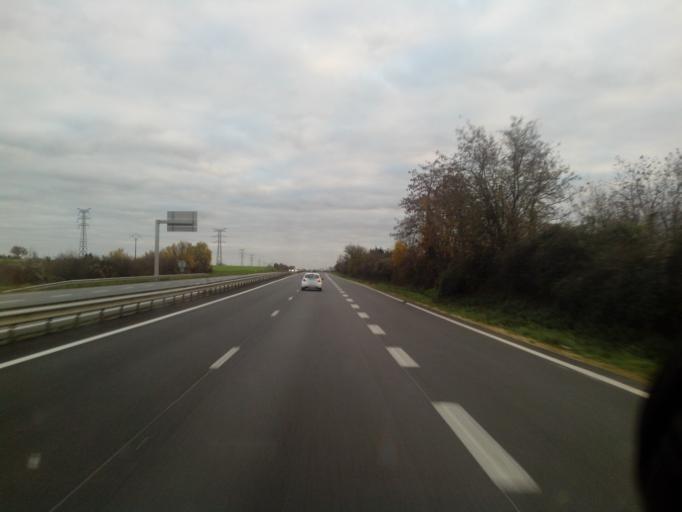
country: FR
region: Poitou-Charentes
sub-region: Departement de la Vienne
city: Montamise
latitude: 46.5960
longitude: 0.3907
